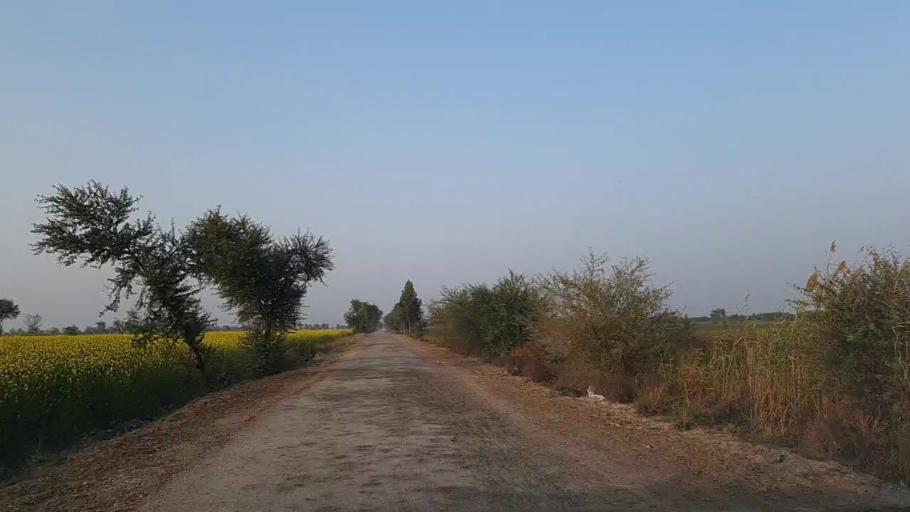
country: PK
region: Sindh
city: Daur
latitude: 26.4221
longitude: 68.3858
